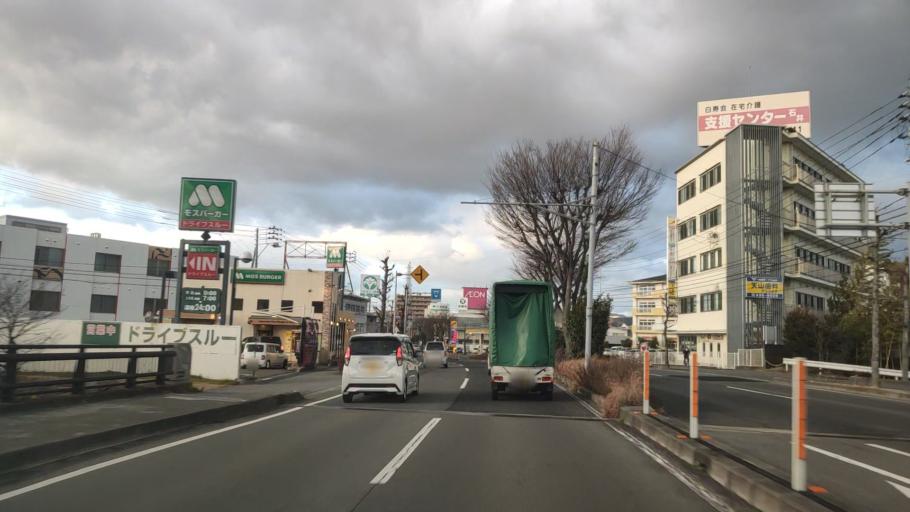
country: JP
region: Ehime
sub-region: Shikoku-chuo Shi
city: Matsuyama
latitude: 33.8178
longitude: 132.7771
